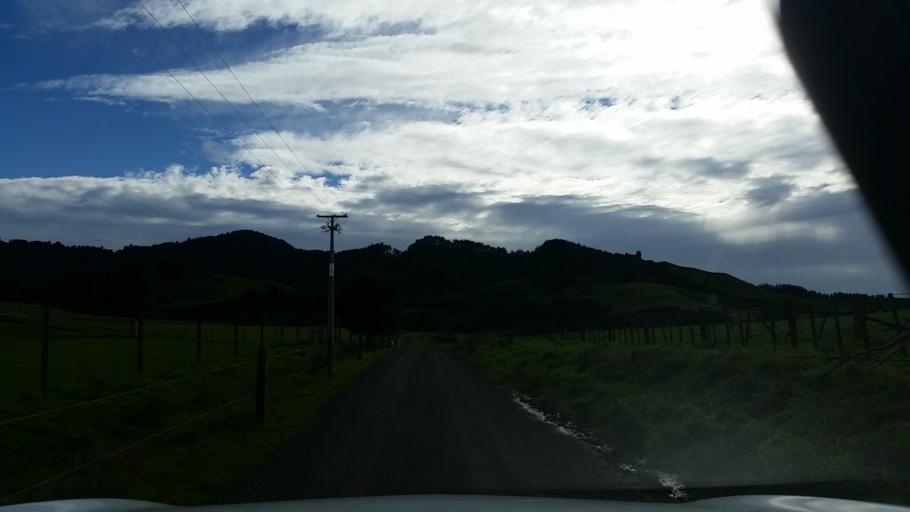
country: NZ
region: Waikato
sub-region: Hauraki District
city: Ngatea
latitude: -37.4989
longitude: 175.4037
